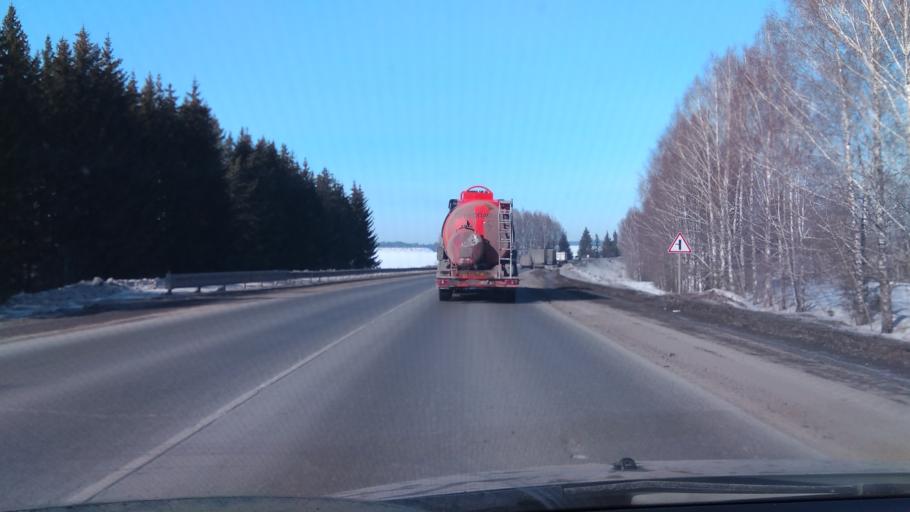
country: RU
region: Perm
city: Kukushtan
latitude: 57.4848
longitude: 56.6729
